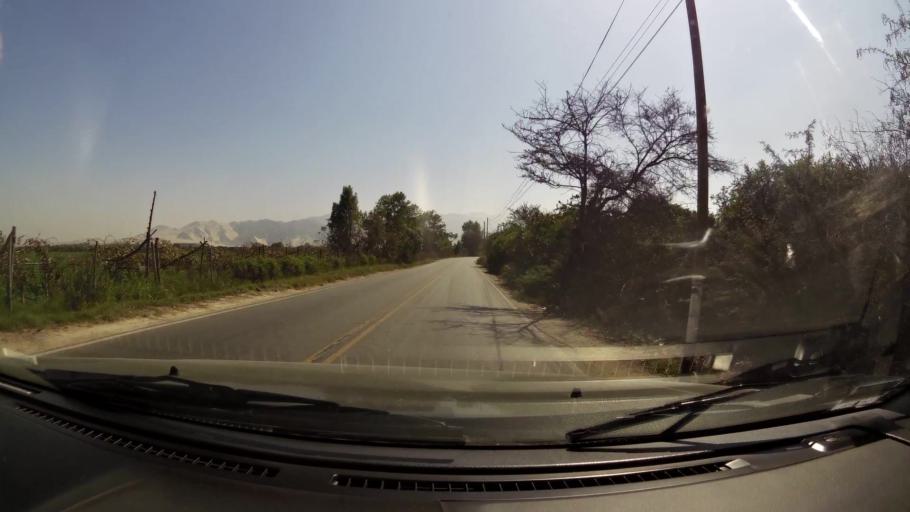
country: PE
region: Ica
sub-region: Provincia de Ica
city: San Juan Bautista
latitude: -13.9750
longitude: -75.6963
